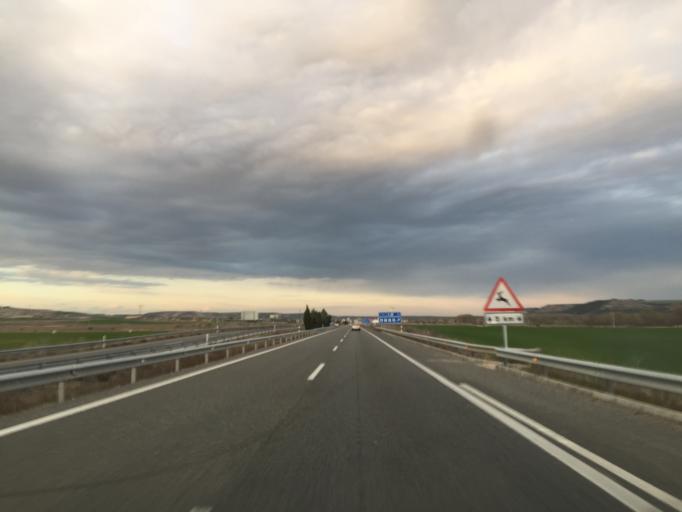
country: ES
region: Castille and Leon
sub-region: Provincia de Burgos
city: Villazopeque
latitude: 42.2057
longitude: -4.0151
